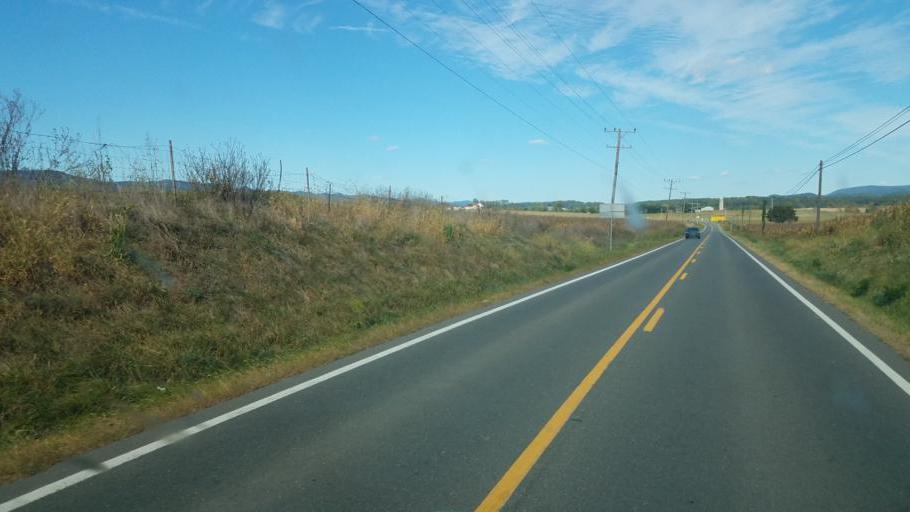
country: US
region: Virginia
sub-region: Page County
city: Luray
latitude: 38.7083
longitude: -78.4366
